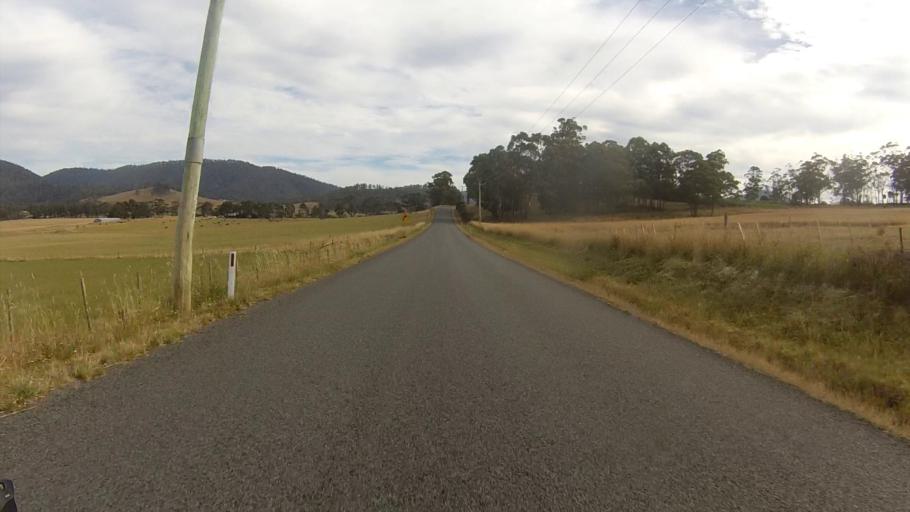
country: AU
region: Tasmania
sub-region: Sorell
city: Sorell
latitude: -42.7989
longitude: 147.7937
